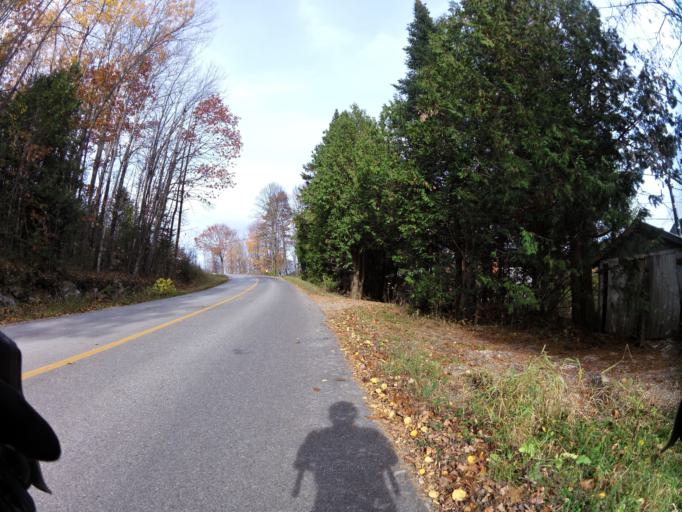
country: CA
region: Quebec
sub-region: Outaouais
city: Wakefield
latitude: 45.7324
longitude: -75.9733
